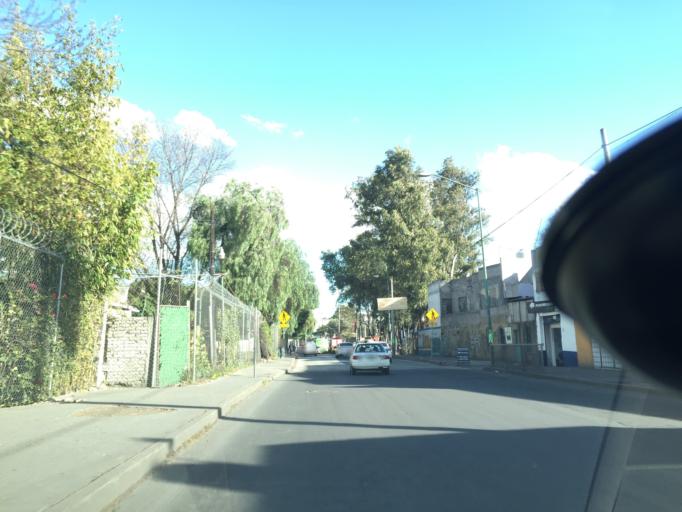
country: MX
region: Mexico City
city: Azcapotzalco
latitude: 19.4884
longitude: -99.1623
